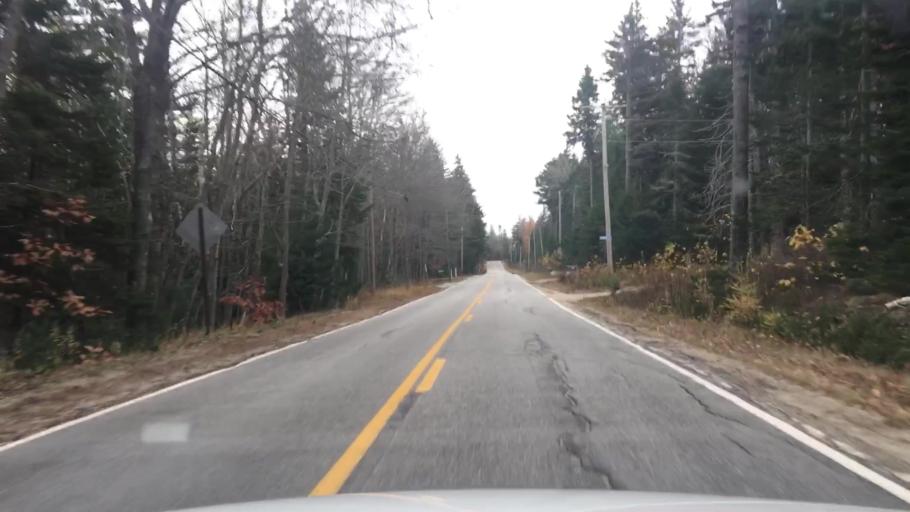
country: US
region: Maine
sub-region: Hancock County
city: Sedgwick
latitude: 44.2994
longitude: -68.5591
